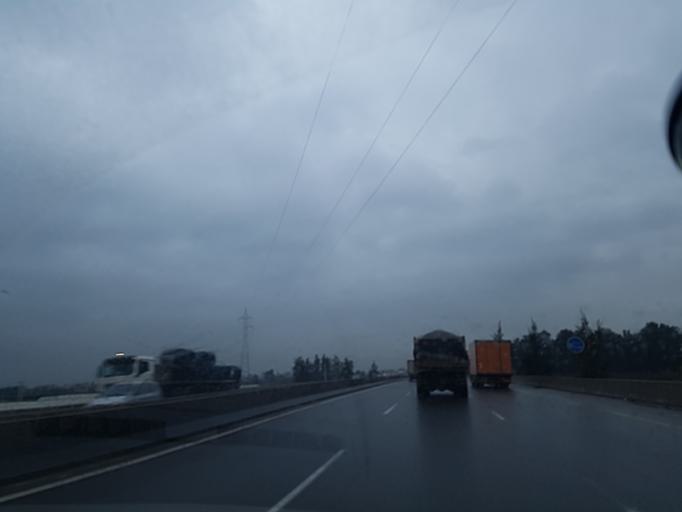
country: DZ
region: Blida
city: Meftah
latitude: 36.6601
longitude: 3.2616
